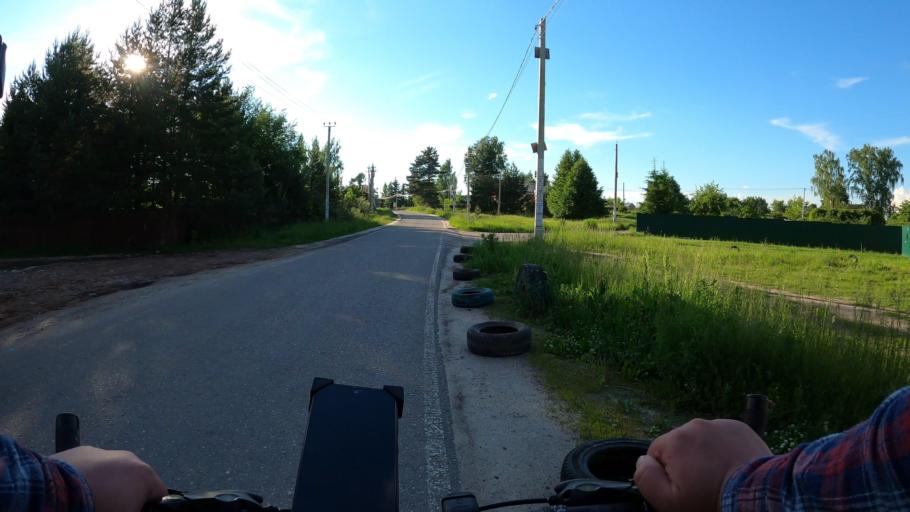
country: RU
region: Moskovskaya
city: Ashitkovo
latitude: 55.4448
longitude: 38.5960
